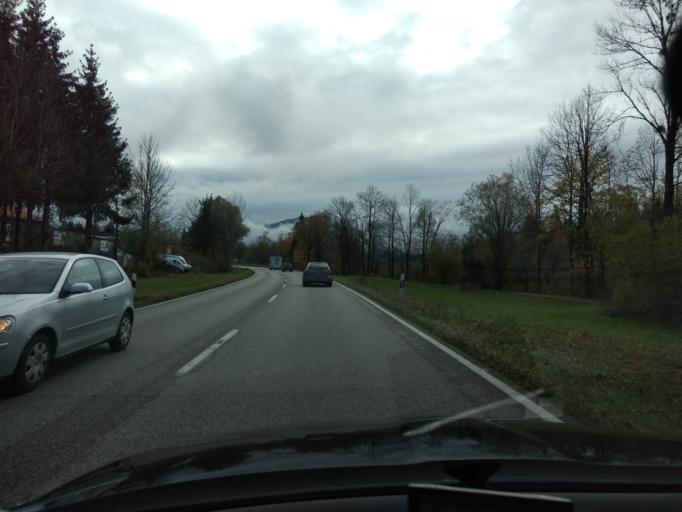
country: DE
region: Bavaria
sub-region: Upper Bavaria
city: Lenggries
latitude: 47.6747
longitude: 11.5720
